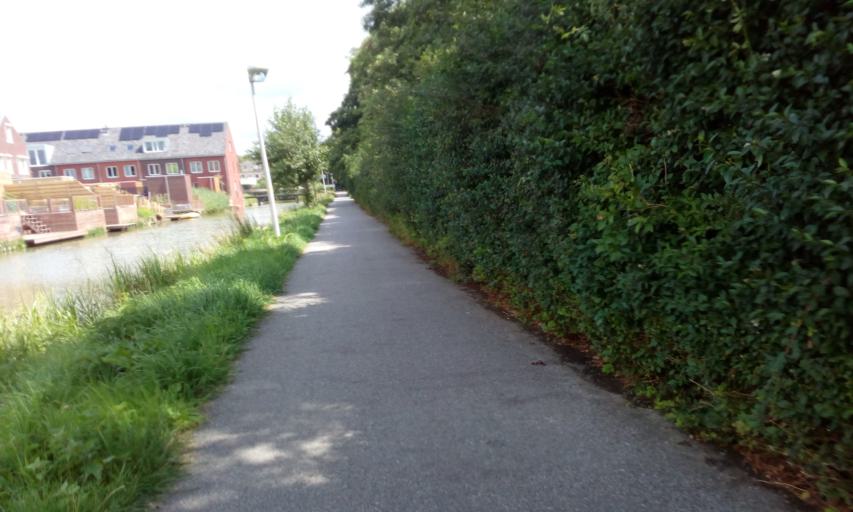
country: NL
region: South Holland
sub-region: Gemeente Delft
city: Delft
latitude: 52.0065
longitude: 4.3297
